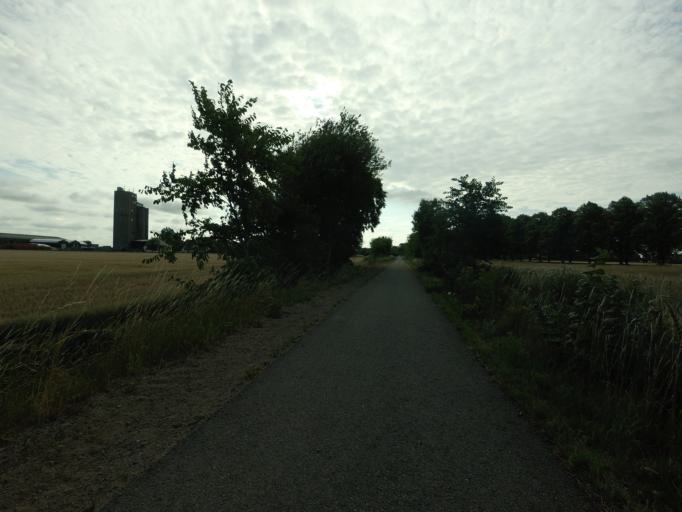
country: SE
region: Skane
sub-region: Helsingborg
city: Odakra
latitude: 56.1779
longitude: 12.6747
